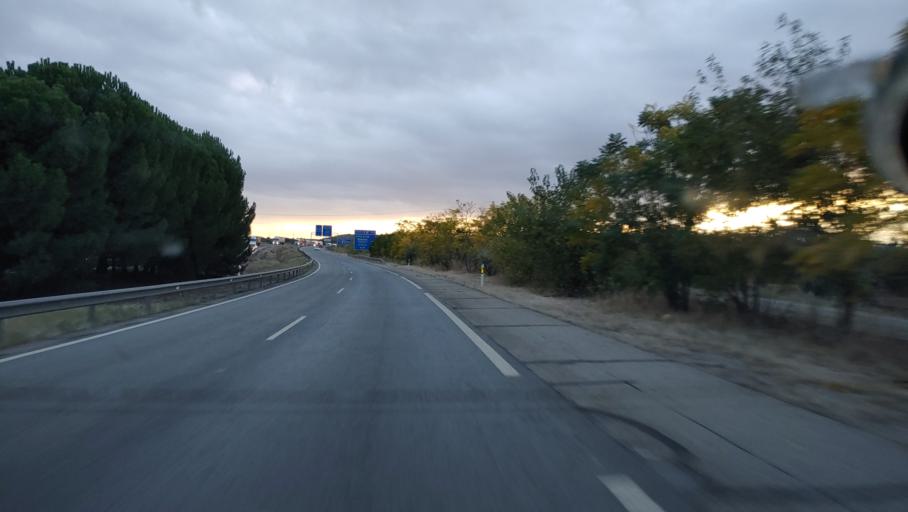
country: ES
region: Andalusia
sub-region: Provincia de Jaen
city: Banos de la Encina
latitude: 38.1373
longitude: -3.7437
